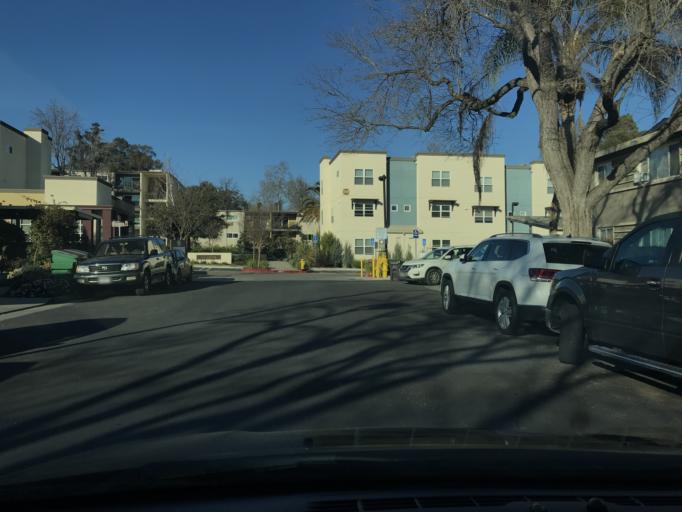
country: US
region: California
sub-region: Santa Clara County
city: Los Gatos
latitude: 37.2307
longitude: -121.9744
